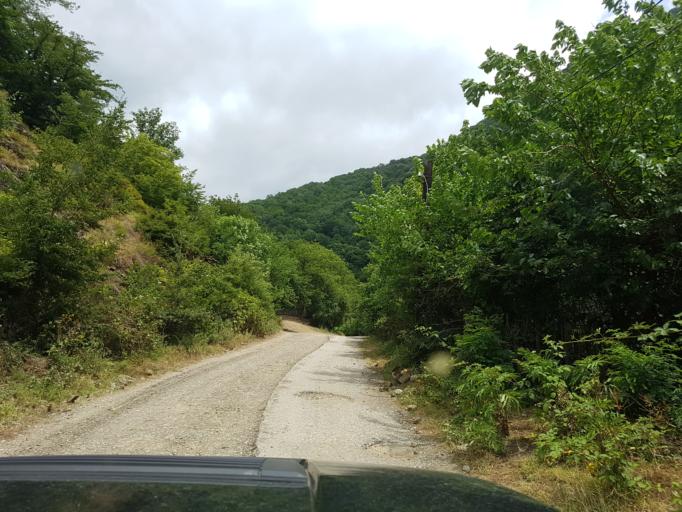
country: GE
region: Imereti
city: Kutaisi
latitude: 42.4374
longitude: 42.7553
